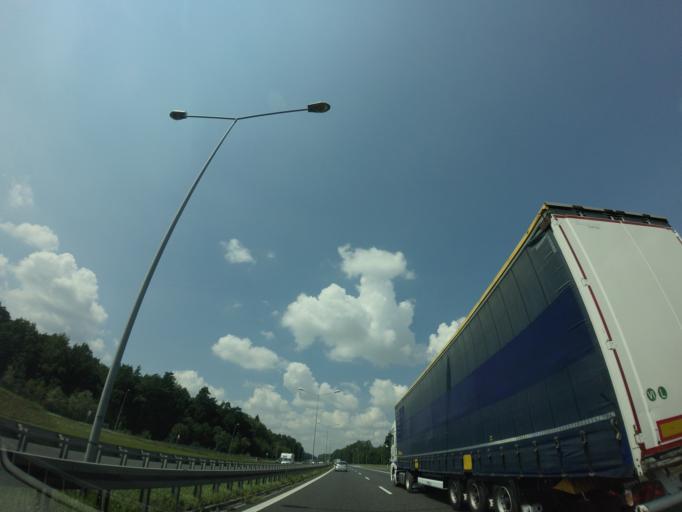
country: PL
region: Opole Voivodeship
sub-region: Powiat strzelecki
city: Ujazd
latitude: 50.4250
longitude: 18.3905
